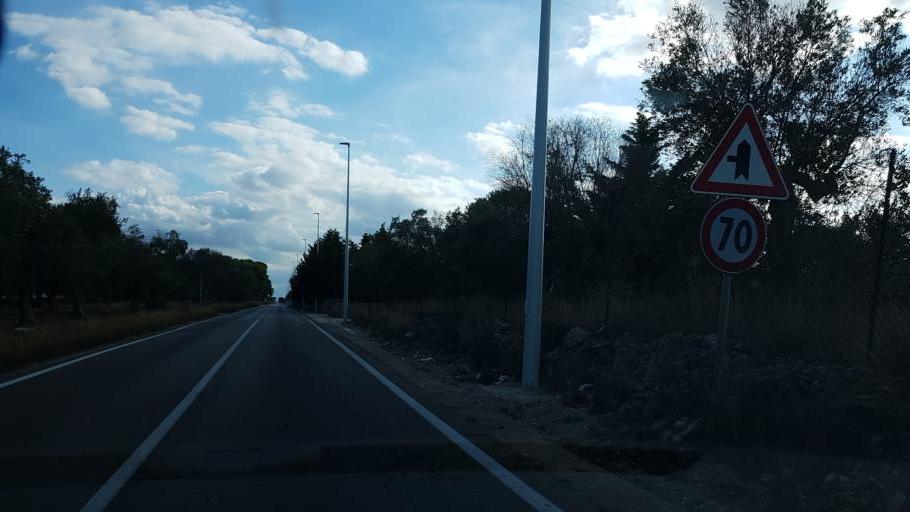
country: IT
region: Apulia
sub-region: Provincia di Lecce
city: Nardo
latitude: 40.1425
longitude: 18.0187
